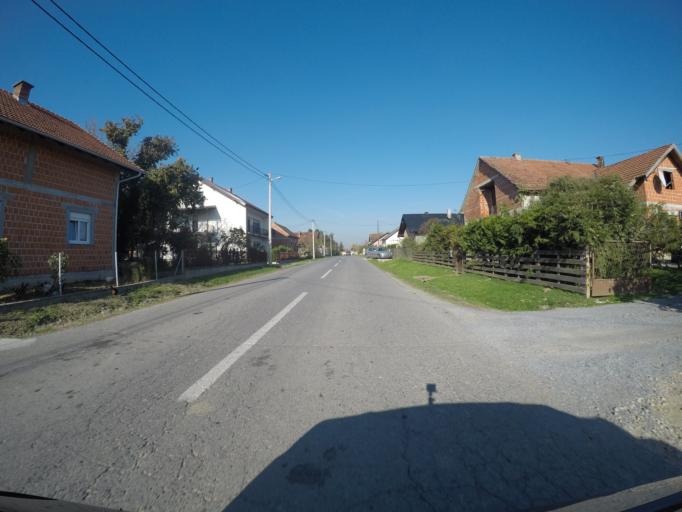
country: HR
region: Bjelovarsko-Bilogorska
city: Predavac
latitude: 45.9086
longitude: 16.7728
